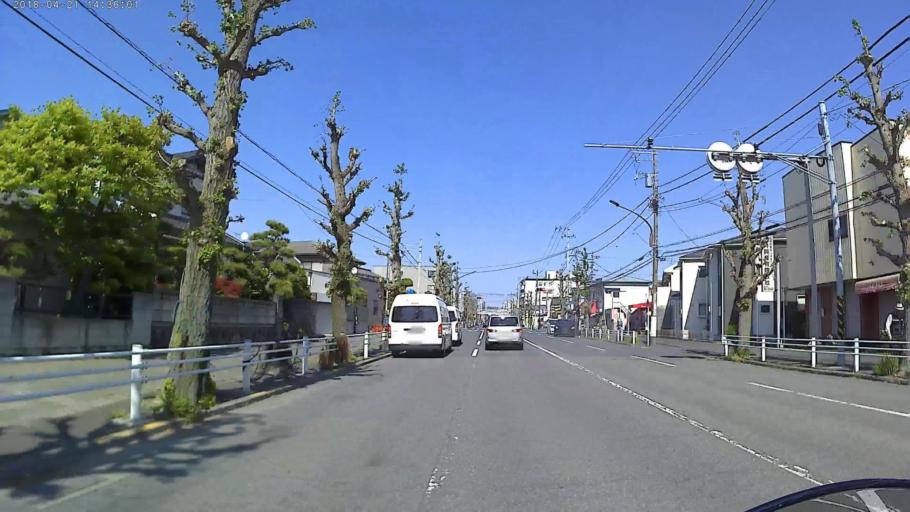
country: JP
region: Kanagawa
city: Hiratsuka
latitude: 35.3259
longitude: 139.3335
